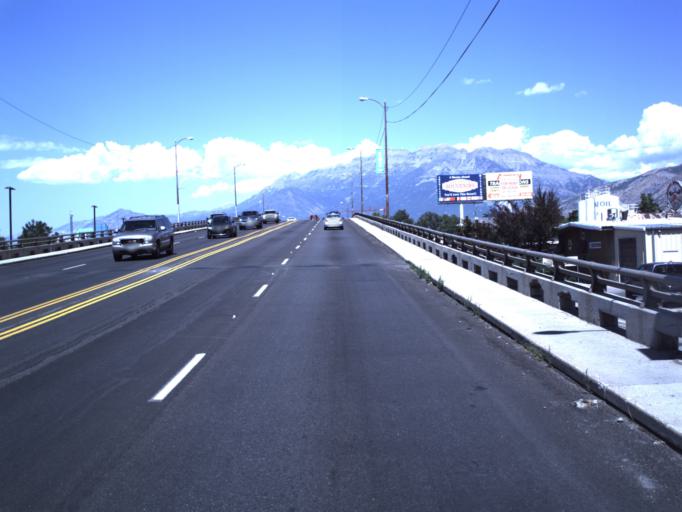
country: US
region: Utah
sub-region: Utah County
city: Provo
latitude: 40.2238
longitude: -111.6587
